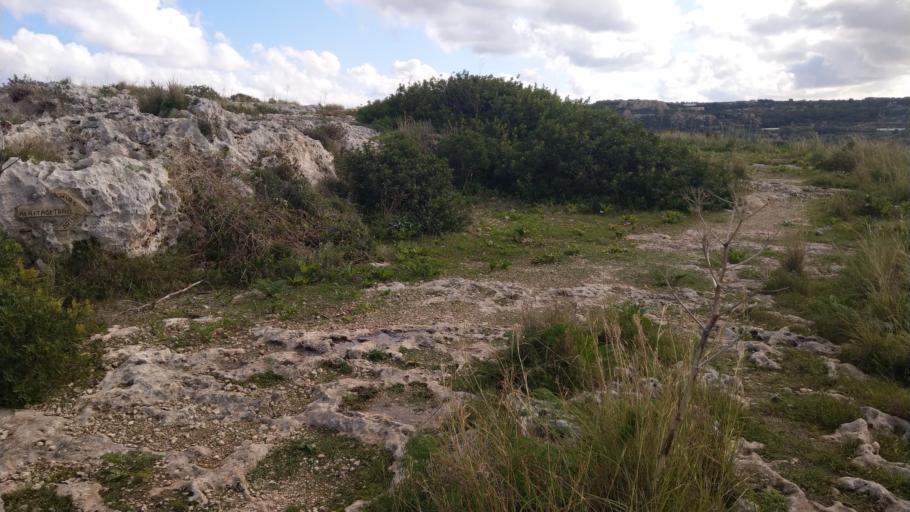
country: MT
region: Il-Mellieha
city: Mellieha
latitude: 35.9498
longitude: 14.3813
